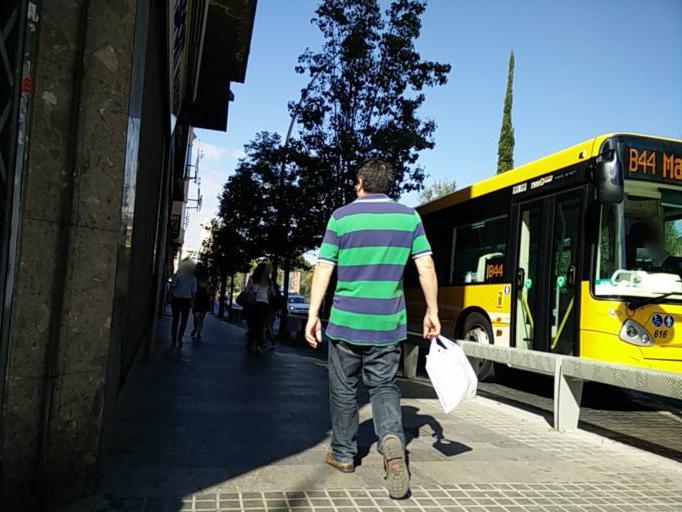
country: ES
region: Catalonia
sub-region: Provincia de Barcelona
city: Badalona
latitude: 41.4492
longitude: 2.2456
